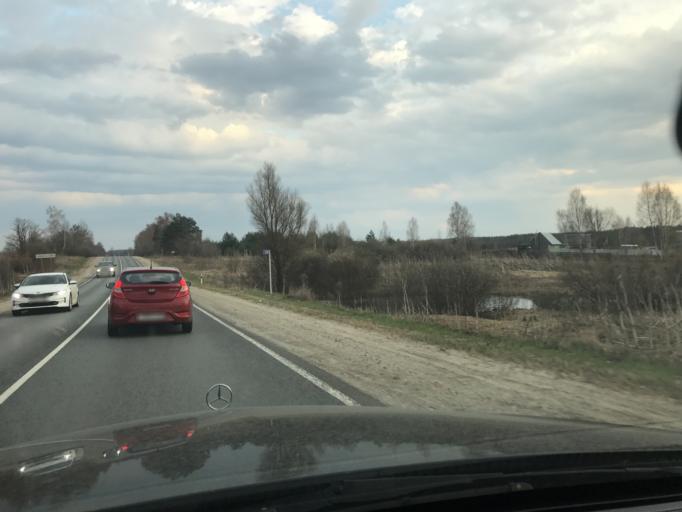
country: RU
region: Vladimir
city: Murom
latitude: 55.6439
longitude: 41.8408
